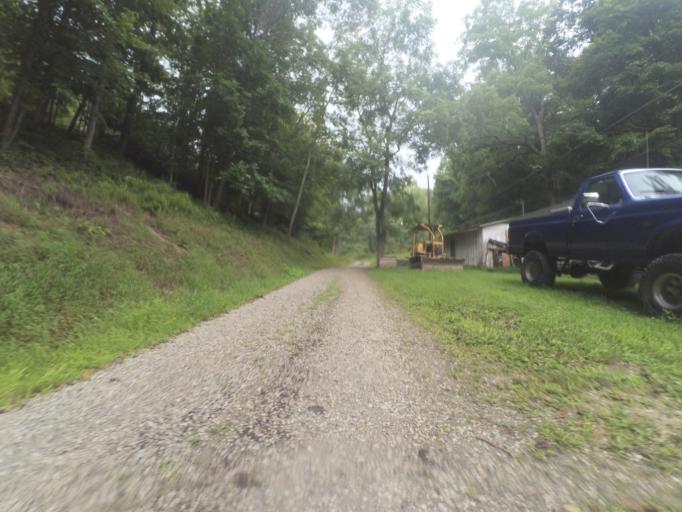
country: US
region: West Virginia
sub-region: Cabell County
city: Huntington
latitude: 38.3758
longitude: -82.3936
